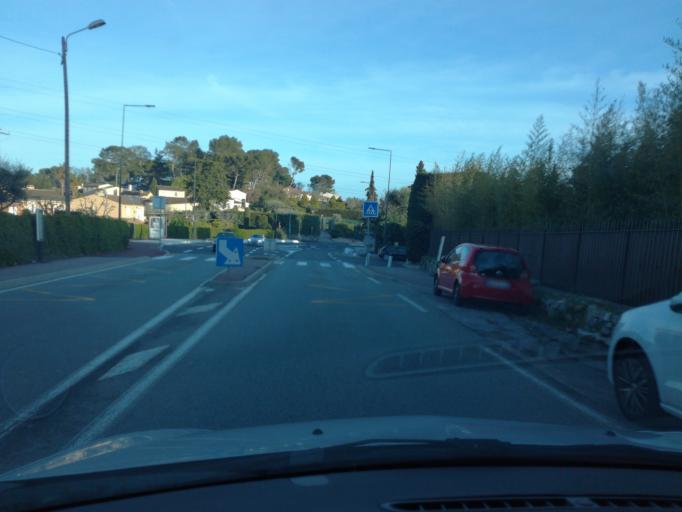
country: FR
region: Provence-Alpes-Cote d'Azur
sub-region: Departement des Alpes-Maritimes
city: Mougins
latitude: 43.6069
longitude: 7.0112
